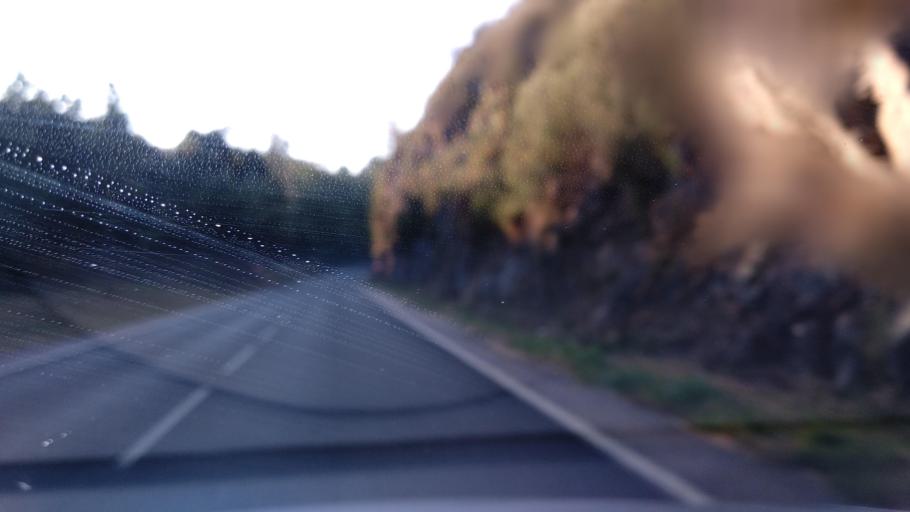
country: ES
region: Galicia
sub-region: Provincia de Pontevedra
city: Ponte Caldelas
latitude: 42.3394
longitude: -8.5547
